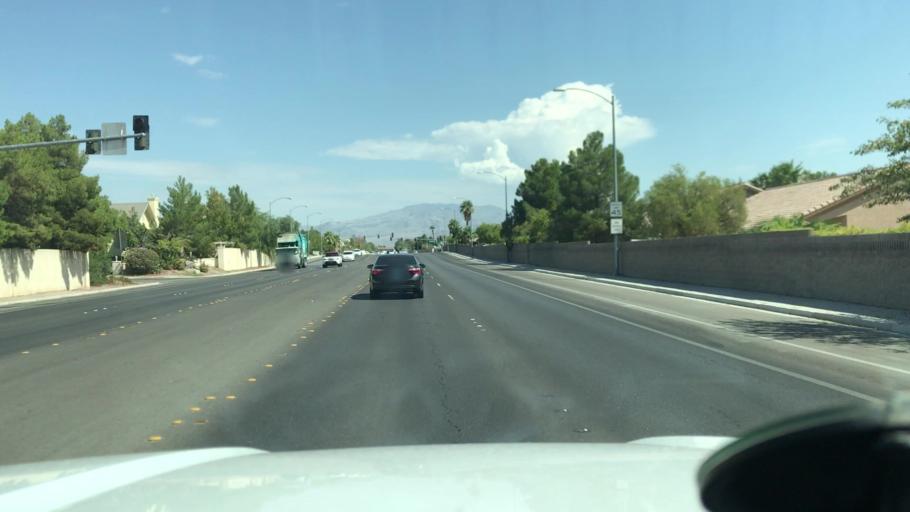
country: US
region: Nevada
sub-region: Clark County
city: Summerlin South
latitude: 36.2600
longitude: -115.2788
